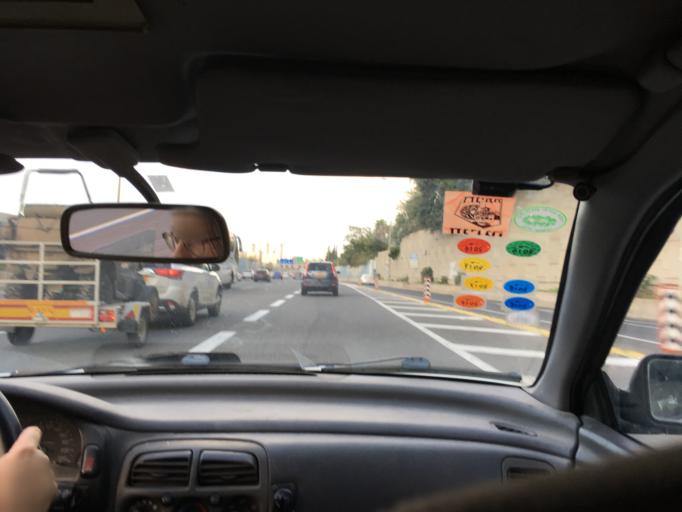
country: IL
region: Tel Aviv
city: Ramat Gan
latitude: 32.0914
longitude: 34.8013
